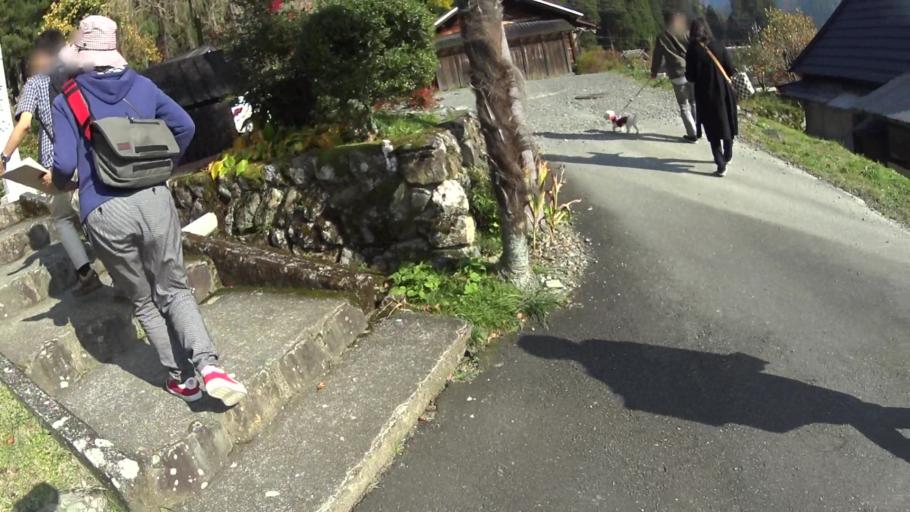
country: JP
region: Fukui
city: Obama
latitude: 35.3145
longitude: 135.6227
